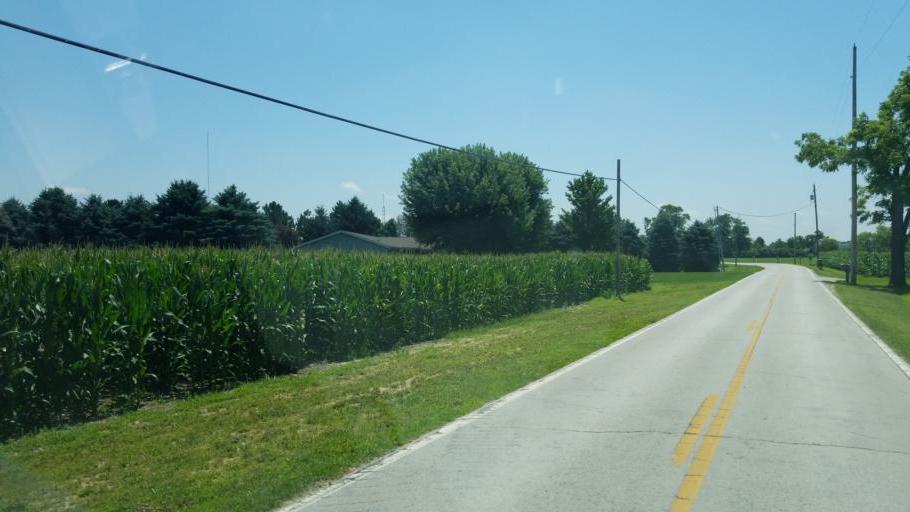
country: US
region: Ohio
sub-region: Sandusky County
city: Fremont
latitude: 41.3719
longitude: -83.0919
